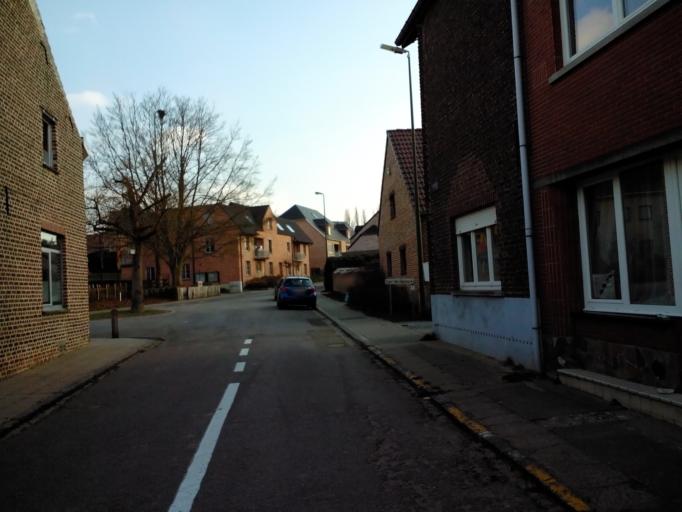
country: BE
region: Flanders
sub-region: Provincie Vlaams-Brabant
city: Oud-Heverlee
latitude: 50.8273
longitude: 4.6896
